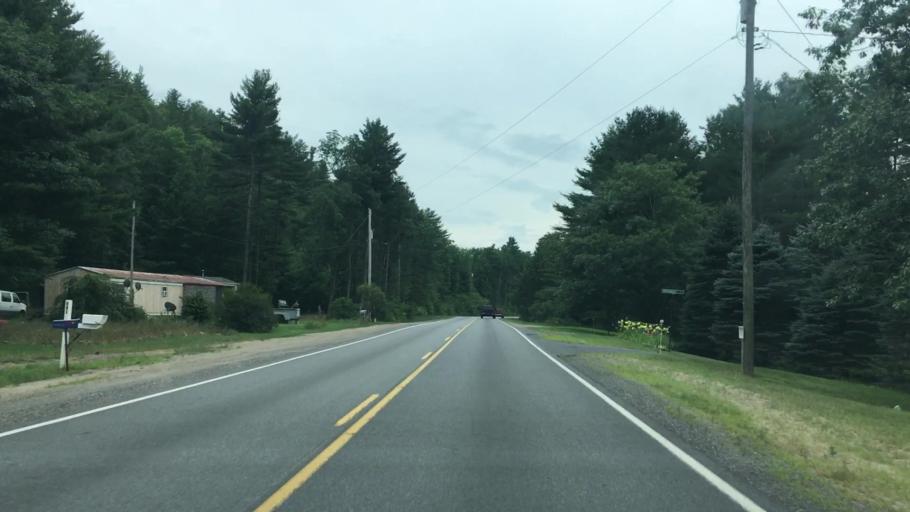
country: US
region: New York
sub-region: Clinton County
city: Peru
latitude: 44.5091
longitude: -73.5835
